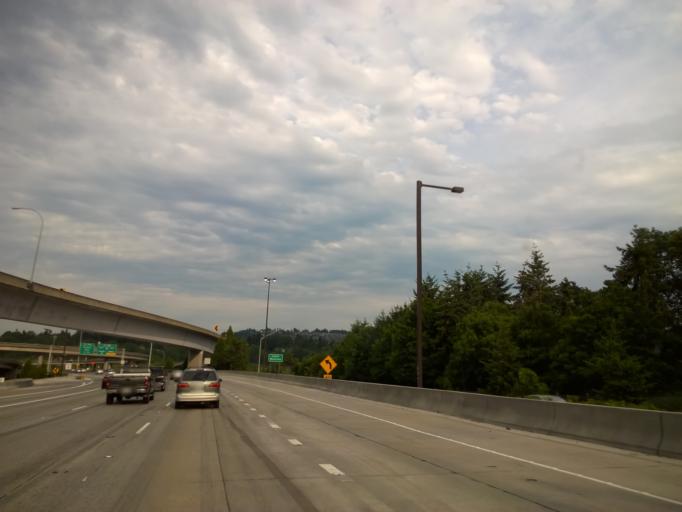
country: US
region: Washington
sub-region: King County
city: Newport
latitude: 47.5791
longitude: -122.1910
